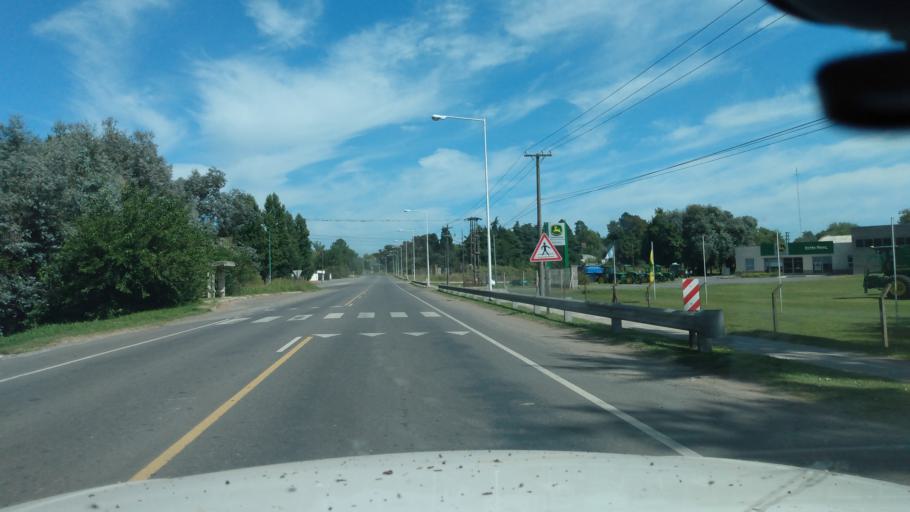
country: AR
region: Buenos Aires
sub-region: Partido de Lujan
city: Lujan
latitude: -34.5496
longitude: -59.1350
